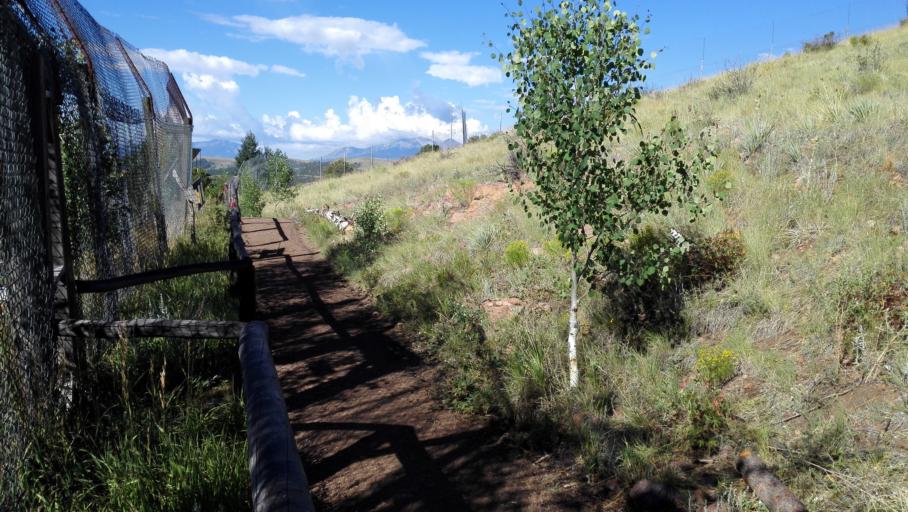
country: US
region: Colorado
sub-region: Custer County
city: Westcliffe
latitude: 37.9639
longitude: -105.2143
